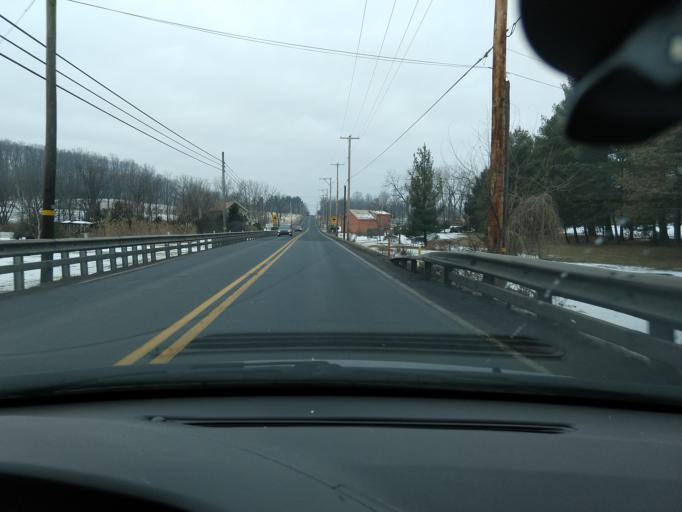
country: US
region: Pennsylvania
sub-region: Lehigh County
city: Macungie
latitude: 40.4757
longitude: -75.5324
